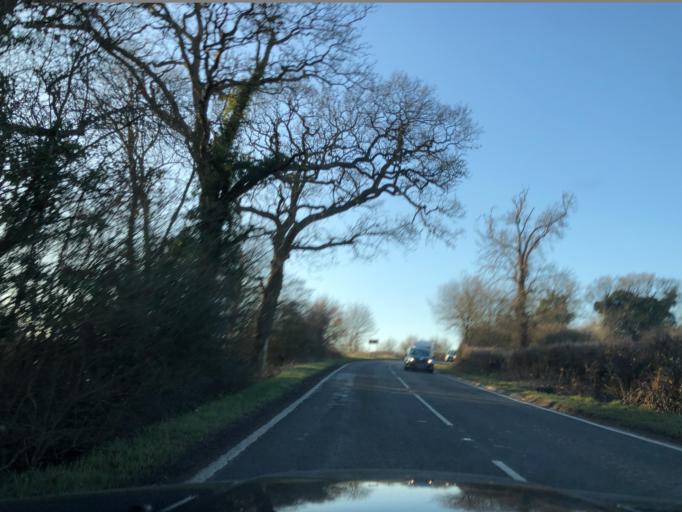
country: GB
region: England
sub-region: Warwickshire
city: Warwick
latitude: 52.2626
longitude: -1.6277
